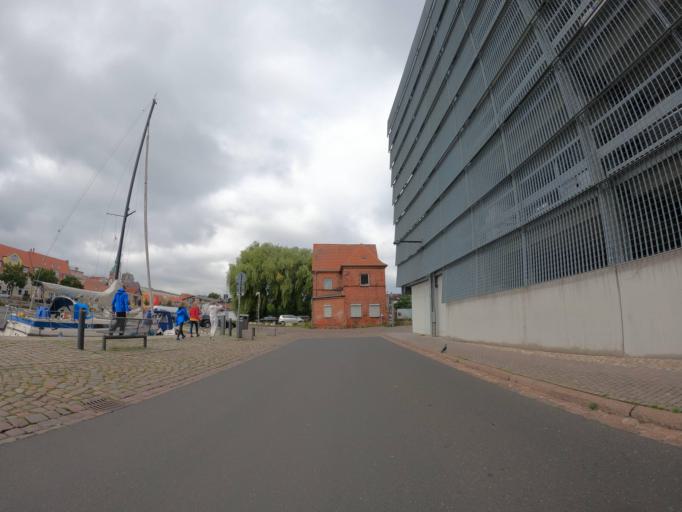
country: DE
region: Mecklenburg-Vorpommern
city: Stralsund
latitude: 54.3132
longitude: 13.0989
